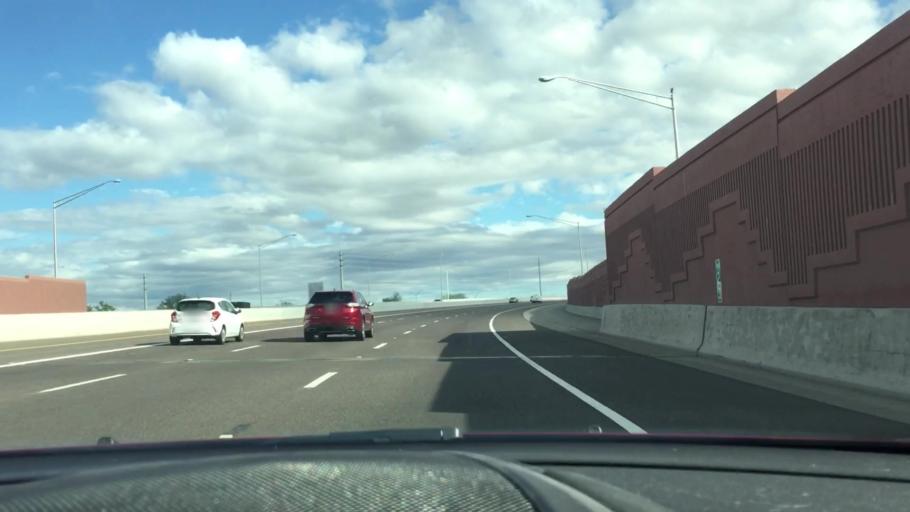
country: US
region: Arizona
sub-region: Maricopa County
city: Fountain Hills
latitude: 33.4745
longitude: -111.6875
